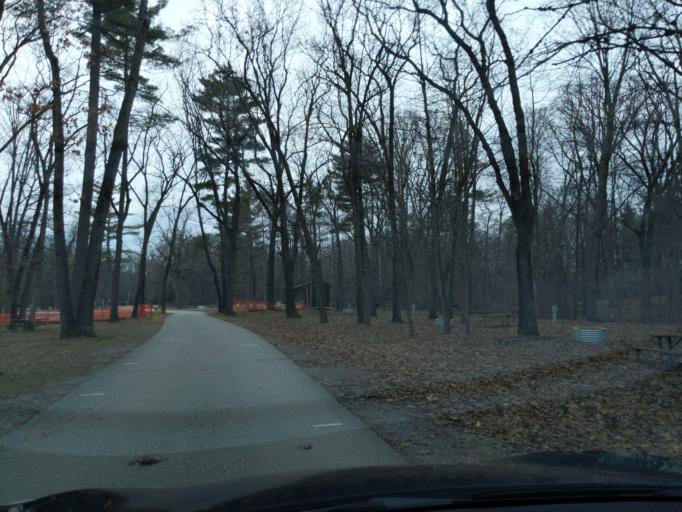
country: US
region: Michigan
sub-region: Bay County
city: Bay City
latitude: 43.6652
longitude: -83.9027
